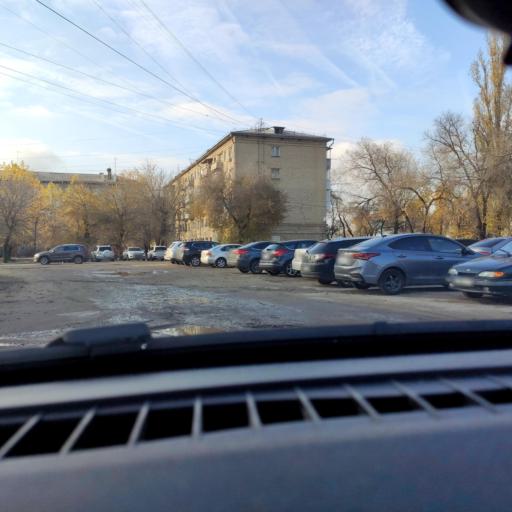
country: RU
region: Voronezj
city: Voronezh
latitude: 51.6354
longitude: 39.2505
